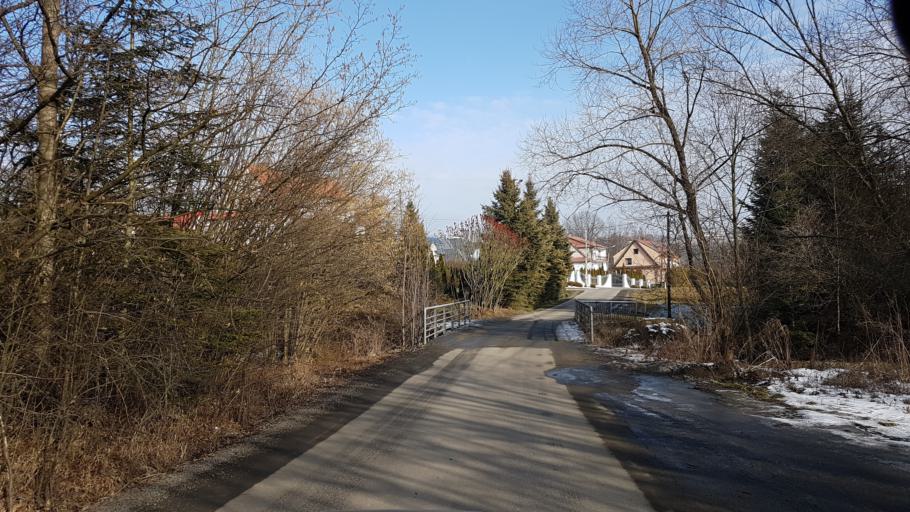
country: PL
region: Lesser Poland Voivodeship
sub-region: Powiat limanowski
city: Lukowica
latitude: 49.6614
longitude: 20.4812
